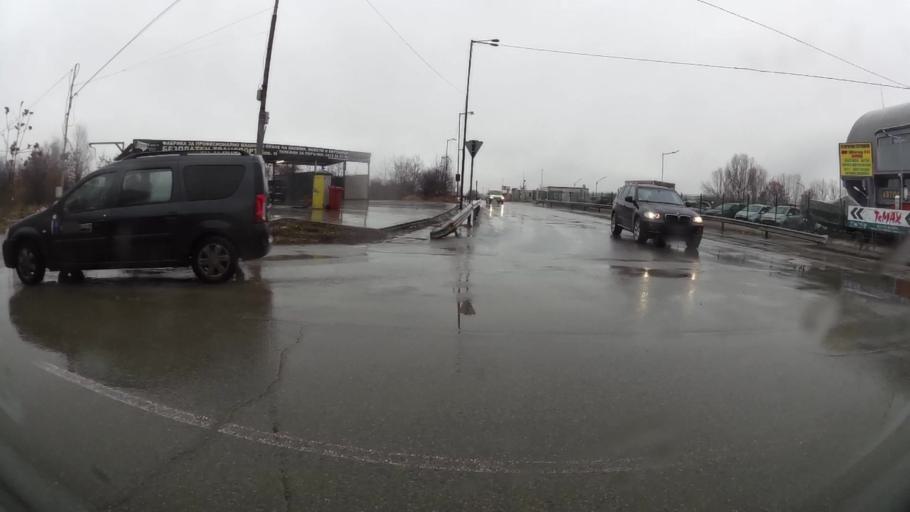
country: BG
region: Sofia-Capital
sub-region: Stolichna Obshtina
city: Sofia
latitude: 42.6394
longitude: 23.3865
